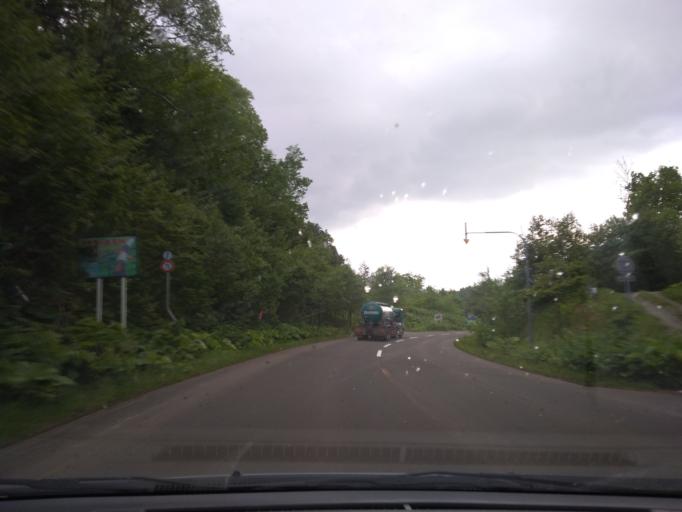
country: JP
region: Hokkaido
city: Shimo-furano
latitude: 43.1328
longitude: 142.4486
